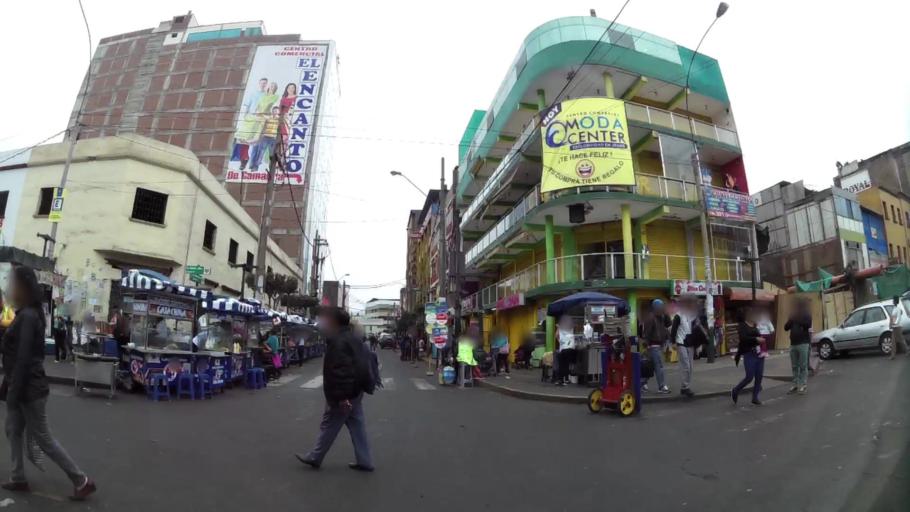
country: PE
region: Lima
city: Lima
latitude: -12.0624
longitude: -77.0137
